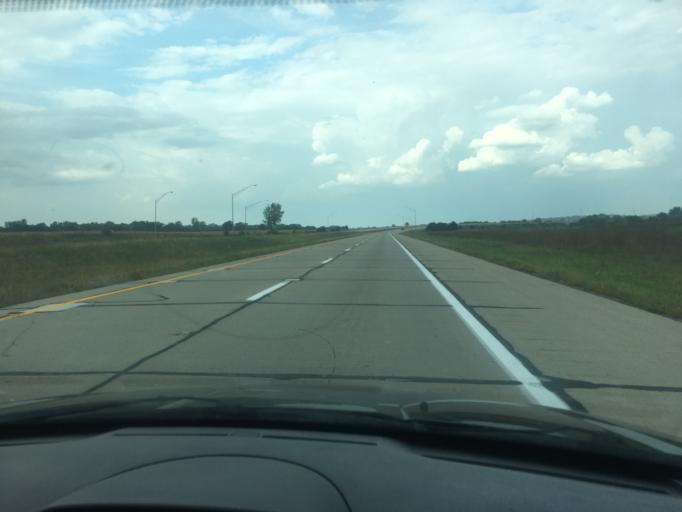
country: US
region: Ohio
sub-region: Clark County
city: Northridge
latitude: 40.0275
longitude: -83.8038
